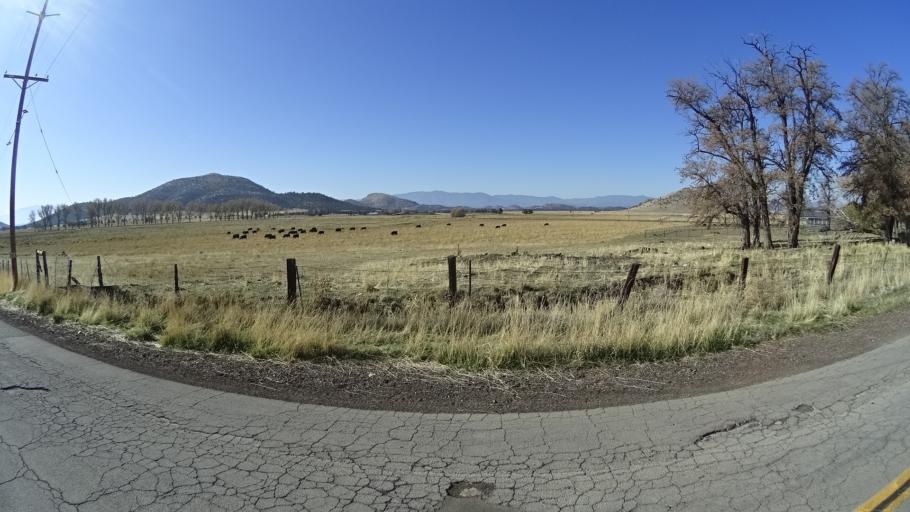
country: US
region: California
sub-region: Siskiyou County
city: Montague
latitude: 41.6889
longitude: -122.3698
